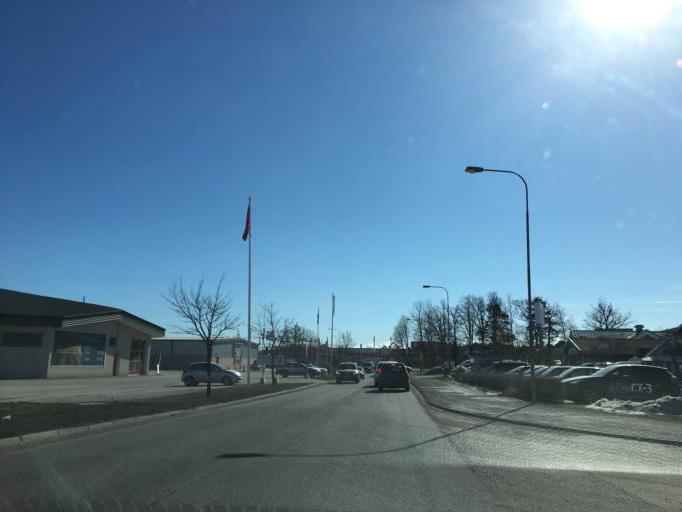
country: SE
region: Vaestmanland
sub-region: Vasteras
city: Vasteras
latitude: 59.6140
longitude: 16.4664
